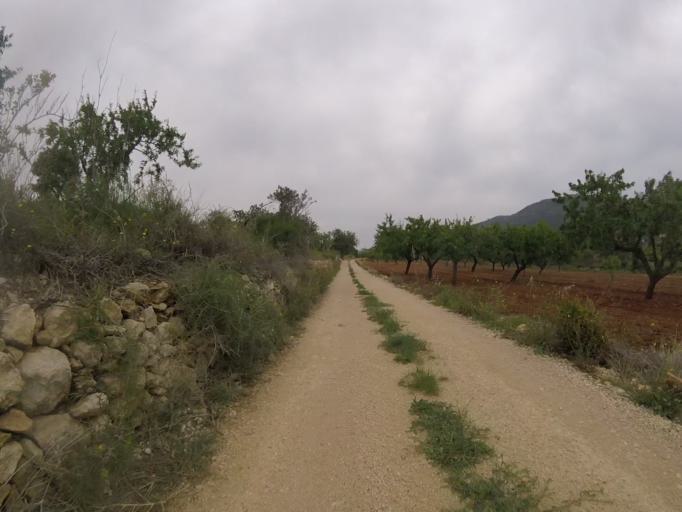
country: ES
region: Valencia
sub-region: Provincia de Castello
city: Alcala de Xivert
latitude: 40.2874
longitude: 0.2581
